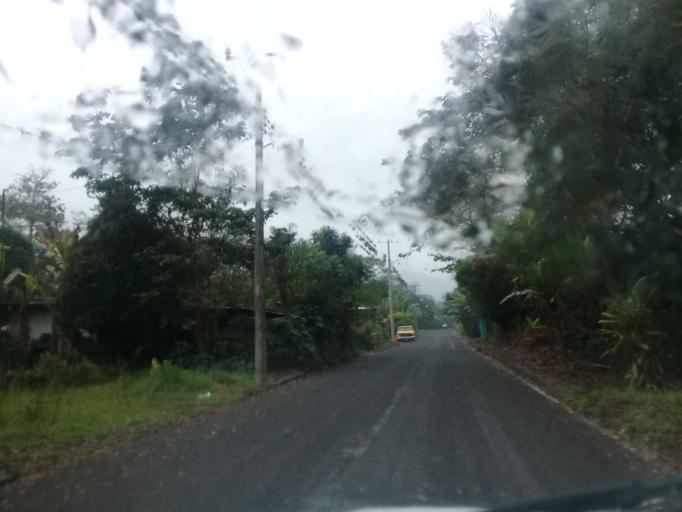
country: MX
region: Veracruz
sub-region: Amatlan de los Reyes
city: Centro de Readaptacion Social
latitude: 18.7999
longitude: -96.9432
